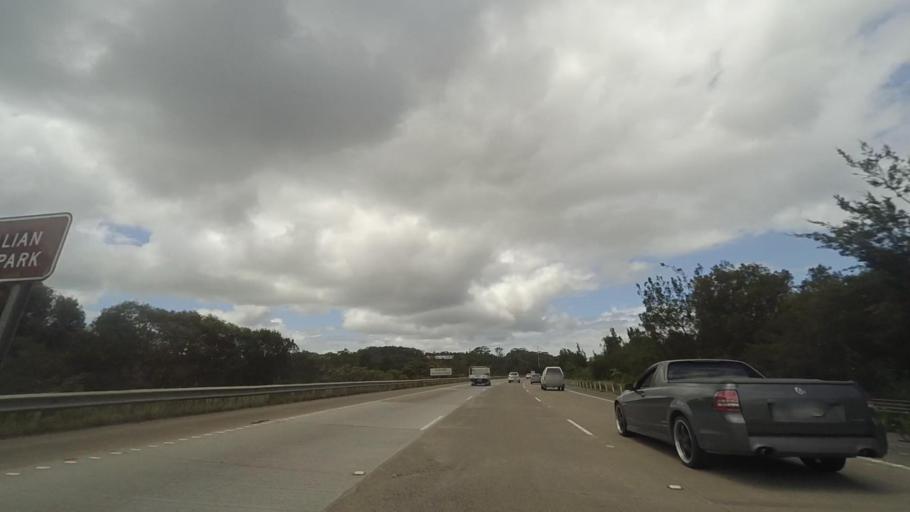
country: AU
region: New South Wales
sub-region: Gosford Shire
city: Point Clare
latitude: -33.4292
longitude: 151.2736
